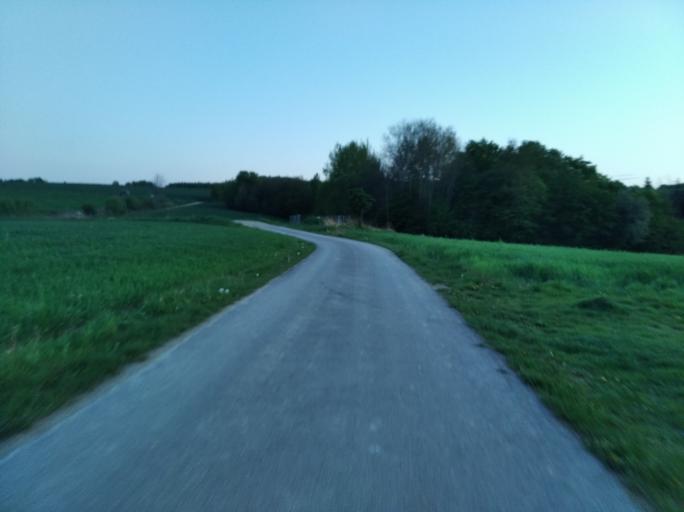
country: PL
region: Subcarpathian Voivodeship
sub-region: Powiat strzyzowski
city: Strzyzow
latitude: 49.9118
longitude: 21.8017
